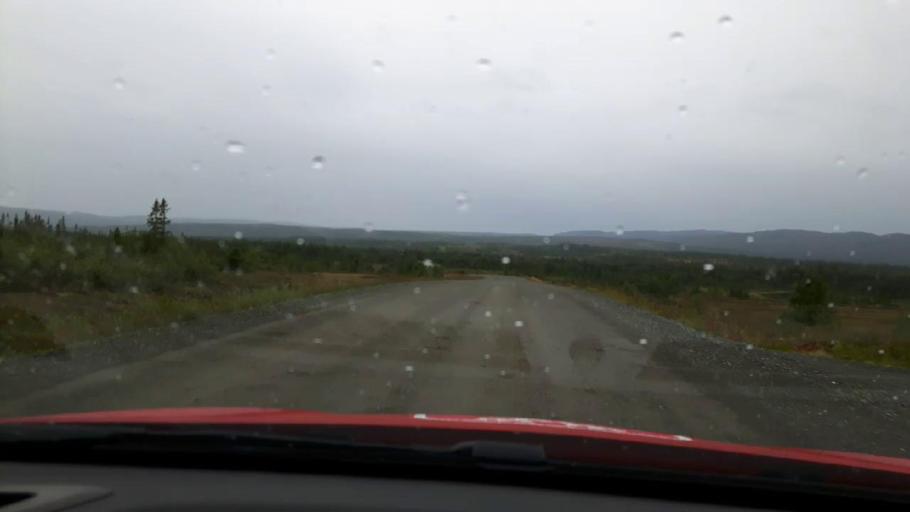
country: NO
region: Nord-Trondelag
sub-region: Meraker
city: Meraker
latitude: 63.5884
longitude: 12.2687
